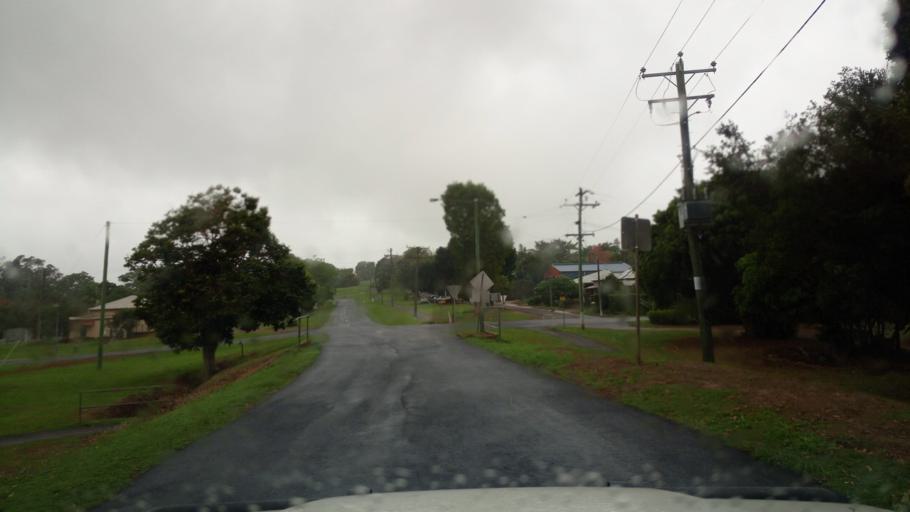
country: AU
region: Queensland
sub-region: Tablelands
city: Tolga
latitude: -17.2698
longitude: 145.5837
